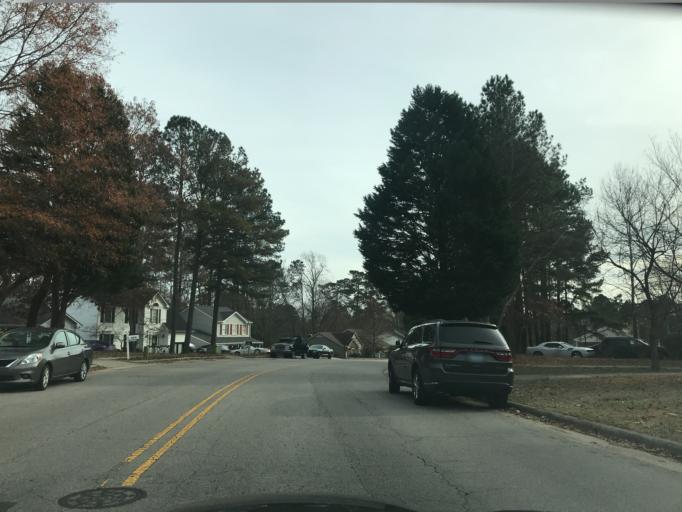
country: US
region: North Carolina
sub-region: Wake County
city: Knightdale
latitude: 35.8523
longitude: -78.5652
